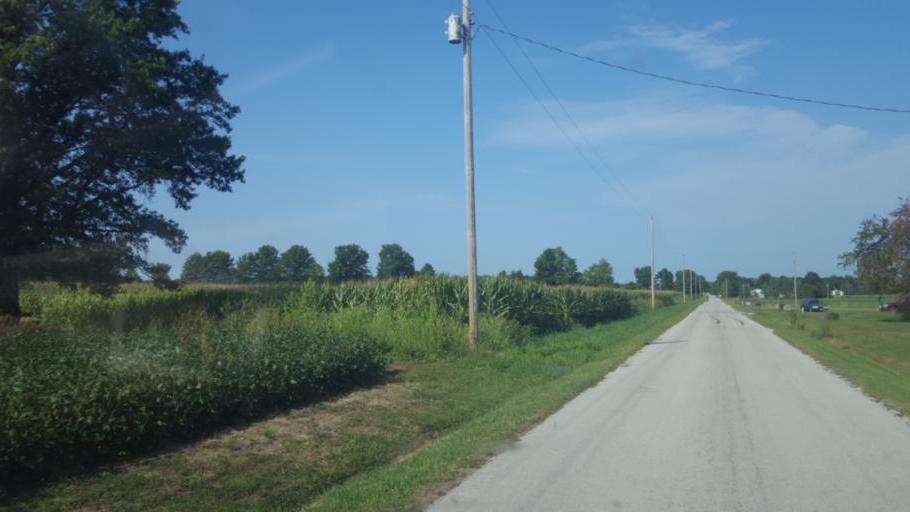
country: US
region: Ohio
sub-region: Morrow County
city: Cardington
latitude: 40.5029
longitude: -82.9334
